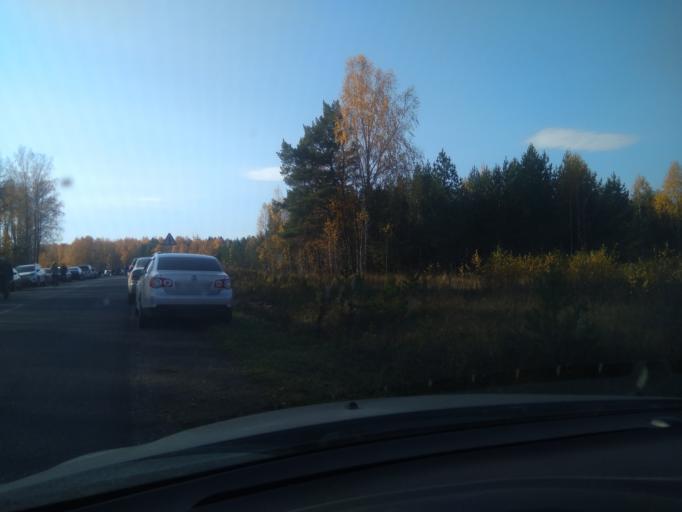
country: RU
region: Sverdlovsk
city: Mikhaylovsk
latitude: 56.5281
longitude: 59.2268
